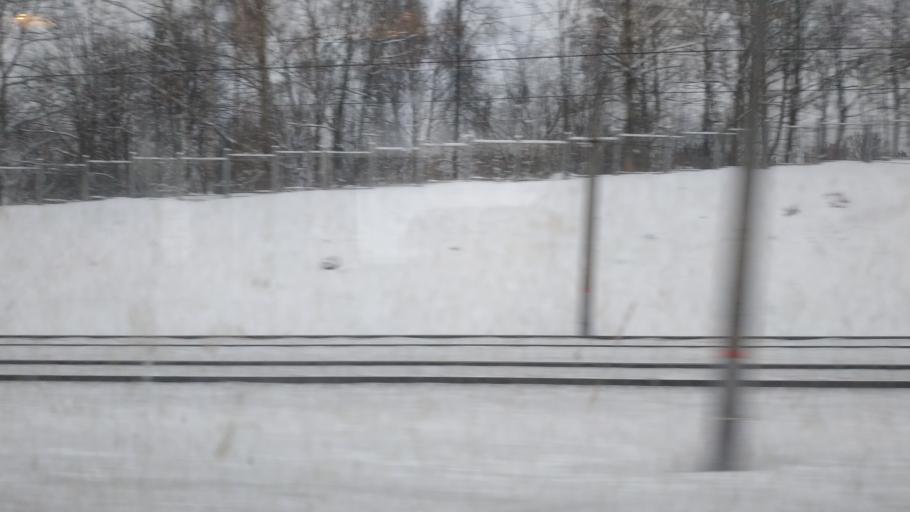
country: RU
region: Moscow
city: Annino
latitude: 55.5525
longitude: 37.5819
